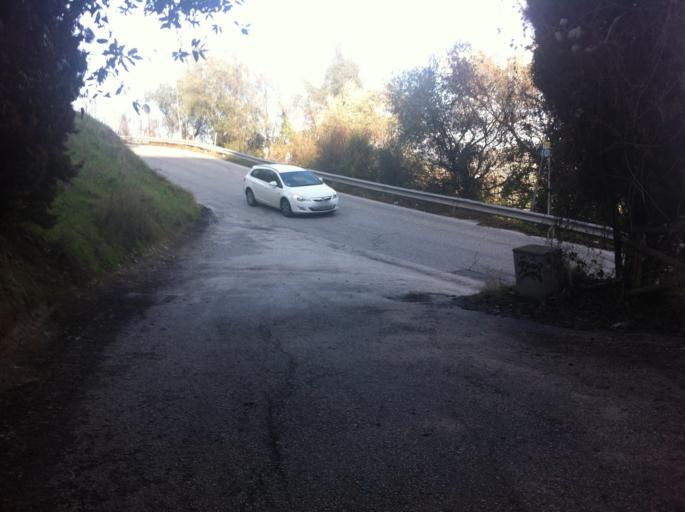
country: IT
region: Umbria
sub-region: Provincia di Perugia
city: Perugia
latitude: 43.1175
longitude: 12.3904
